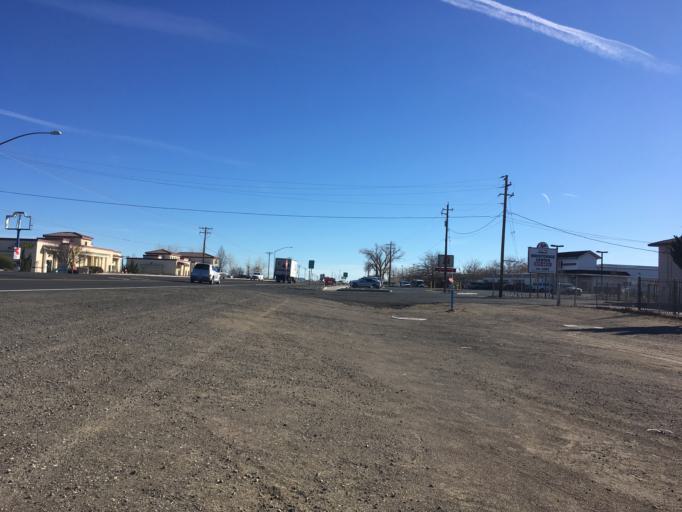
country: US
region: Nevada
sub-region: Lyon County
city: Fernley
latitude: 39.6074
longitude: -119.2438
